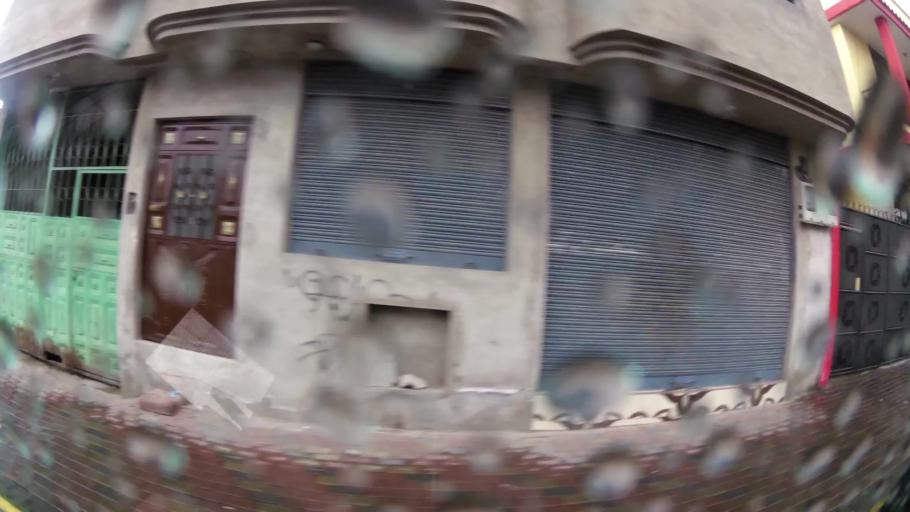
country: EC
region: Pichincha
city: Quito
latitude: -0.3206
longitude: -78.5502
